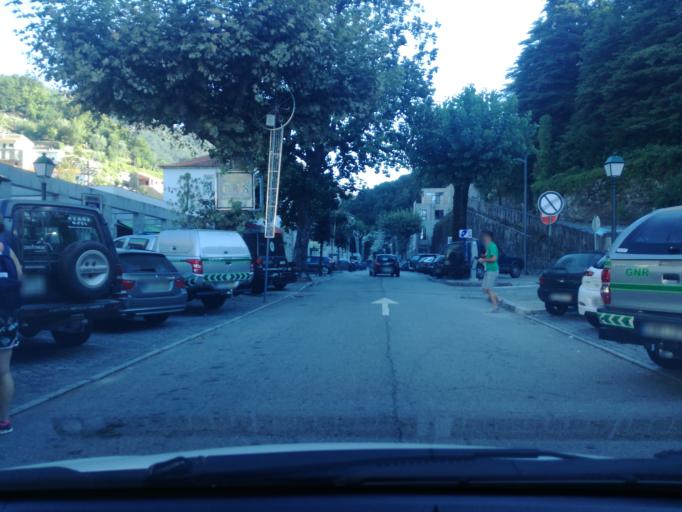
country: PT
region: Braga
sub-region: Vieira do Minho
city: Real
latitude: 41.7269
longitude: -8.1626
